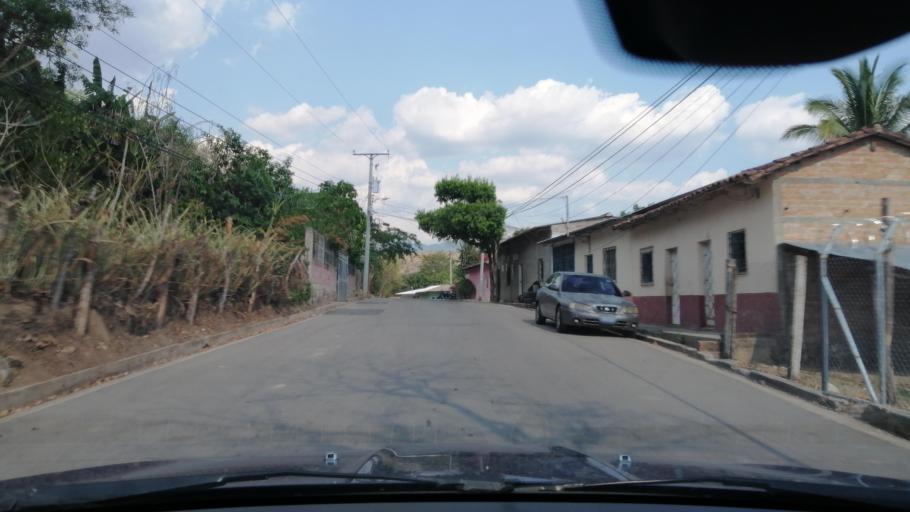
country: SV
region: Santa Ana
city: Metapan
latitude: 14.3293
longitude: -89.4298
